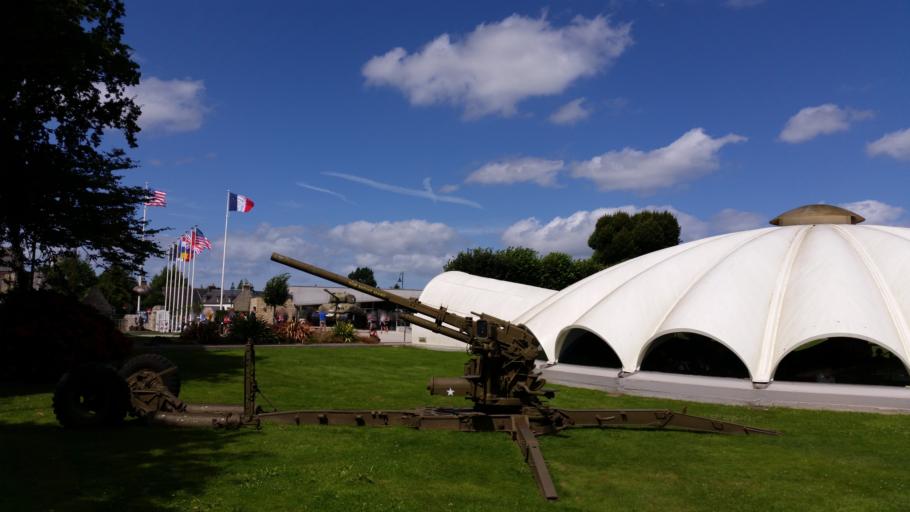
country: FR
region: Lower Normandy
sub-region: Departement de la Manche
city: Sainte-Mere-Eglise
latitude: 49.4078
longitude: -1.3149
